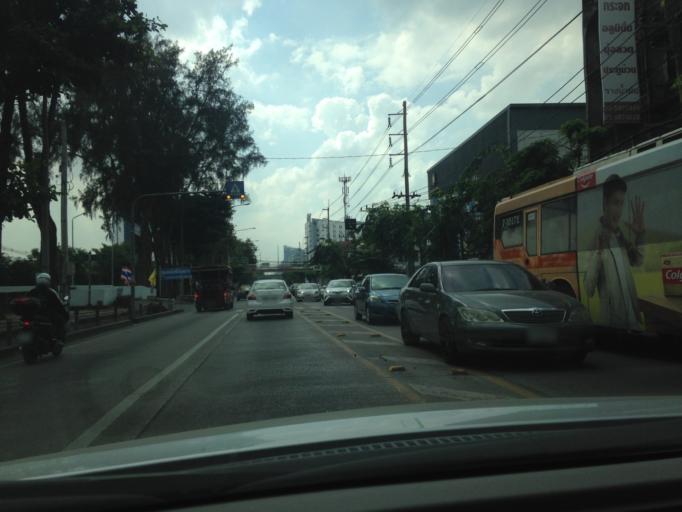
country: TH
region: Bangkok
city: Chatuchak
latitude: 13.8367
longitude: 100.5406
